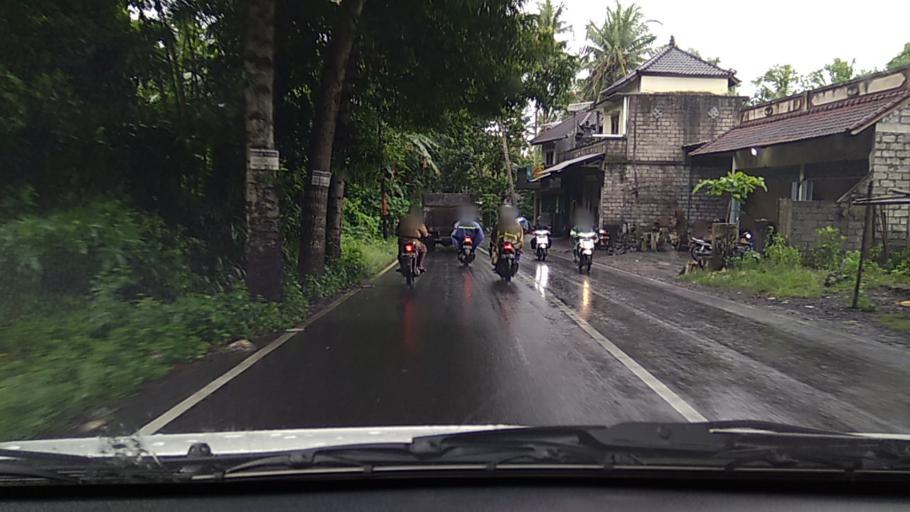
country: ID
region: Bali
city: Banjar Timbrah
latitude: -8.4800
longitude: 115.6103
